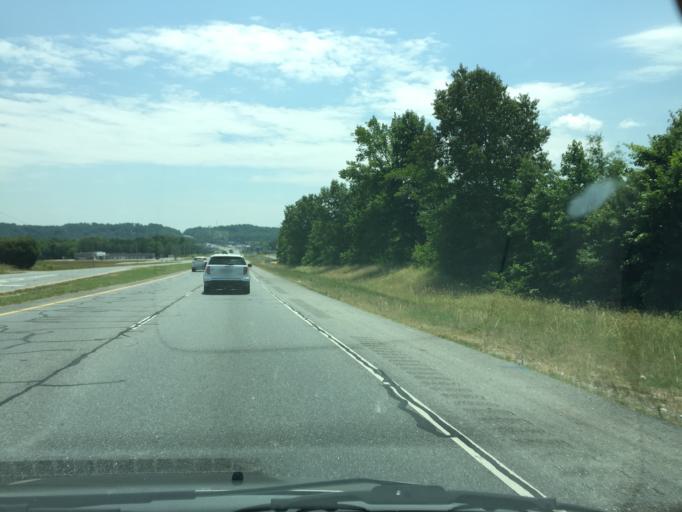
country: US
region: Georgia
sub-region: Catoosa County
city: Indian Springs
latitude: 34.9340
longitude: -85.1920
